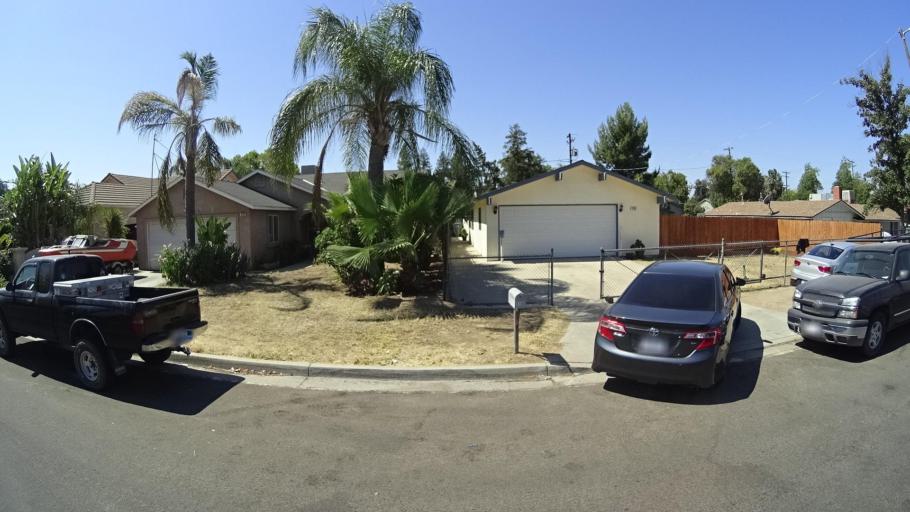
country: US
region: California
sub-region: Fresno County
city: Fresno
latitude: 36.7605
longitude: -119.7378
